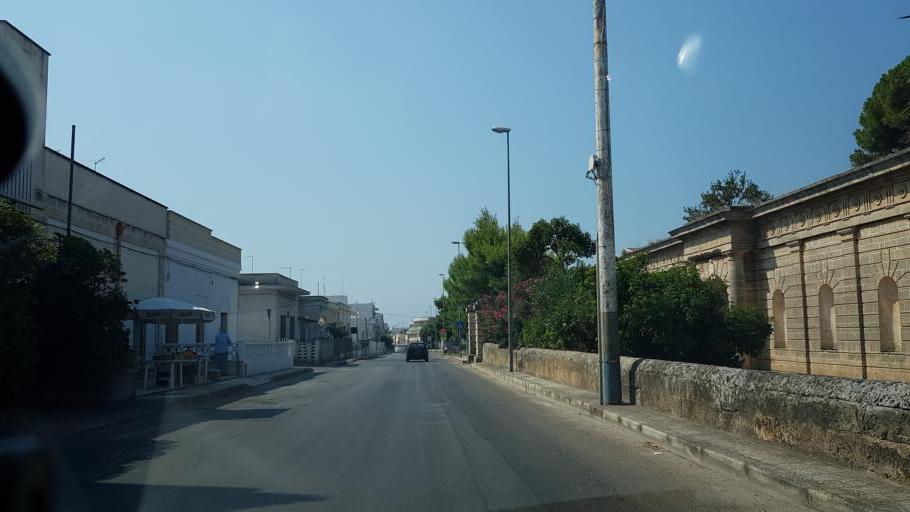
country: IT
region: Apulia
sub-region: Provincia di Taranto
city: Maruggio
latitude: 40.3280
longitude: 17.5737
